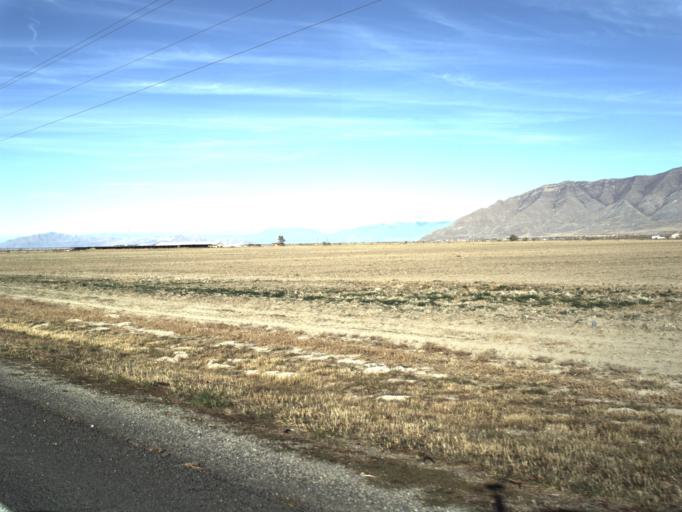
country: US
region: Utah
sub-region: Tooele County
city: Erda
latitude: 40.6025
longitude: -112.3707
